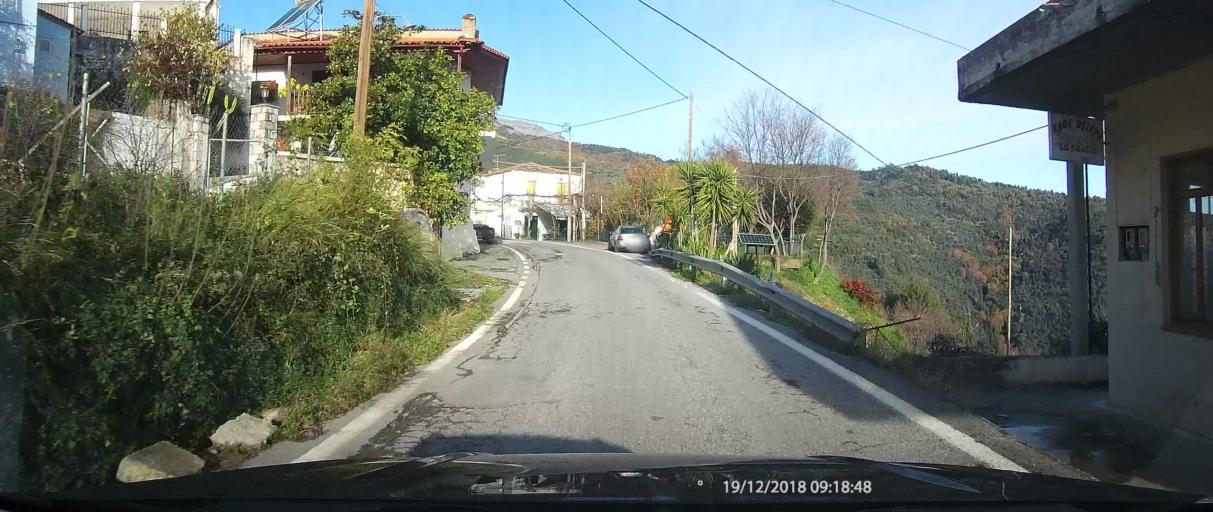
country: GR
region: Peloponnese
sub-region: Nomos Lakonias
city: Magoula
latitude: 37.0933
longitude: 22.3501
